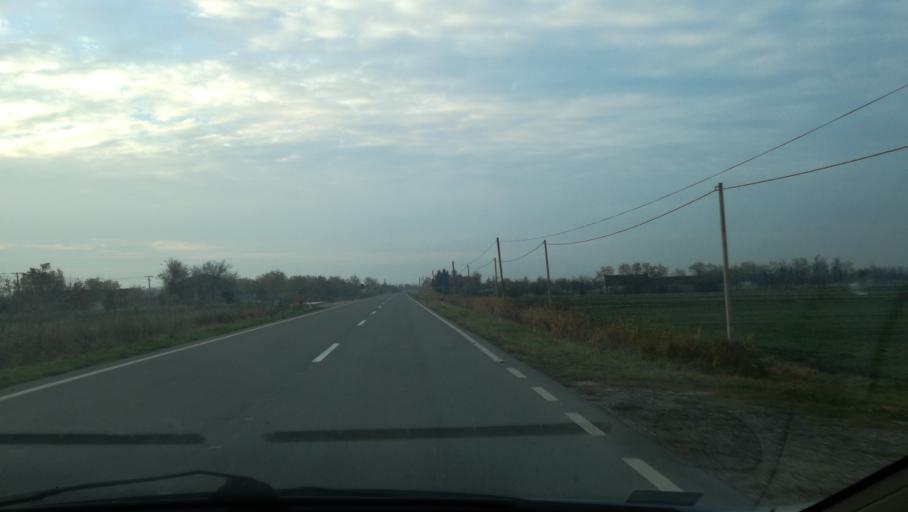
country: RS
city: Banatska Topola
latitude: 45.6886
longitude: 20.4229
